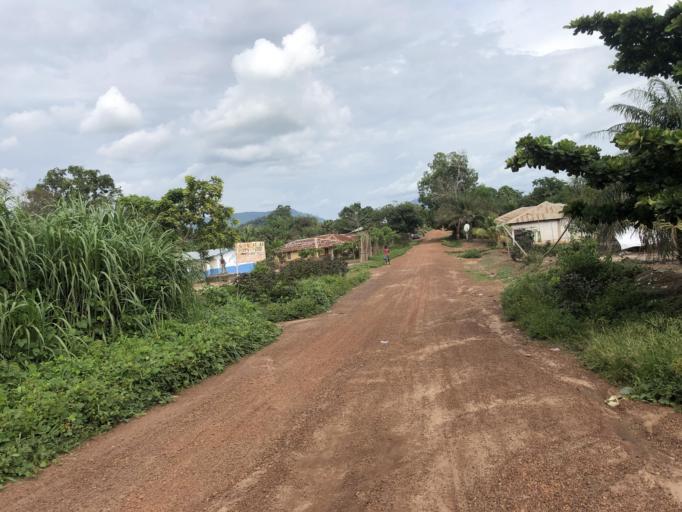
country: SL
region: Northern Province
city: Masaka
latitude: 8.7500
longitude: -11.8432
